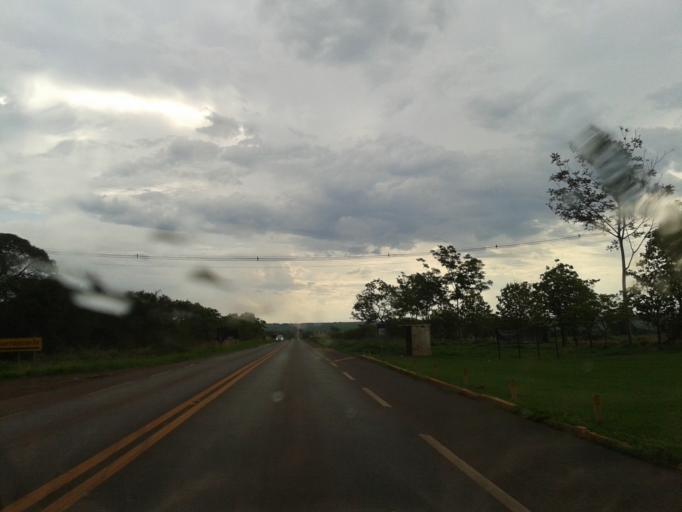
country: BR
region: Minas Gerais
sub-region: Ituiutaba
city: Ituiutaba
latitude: -18.9657
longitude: -49.5019
